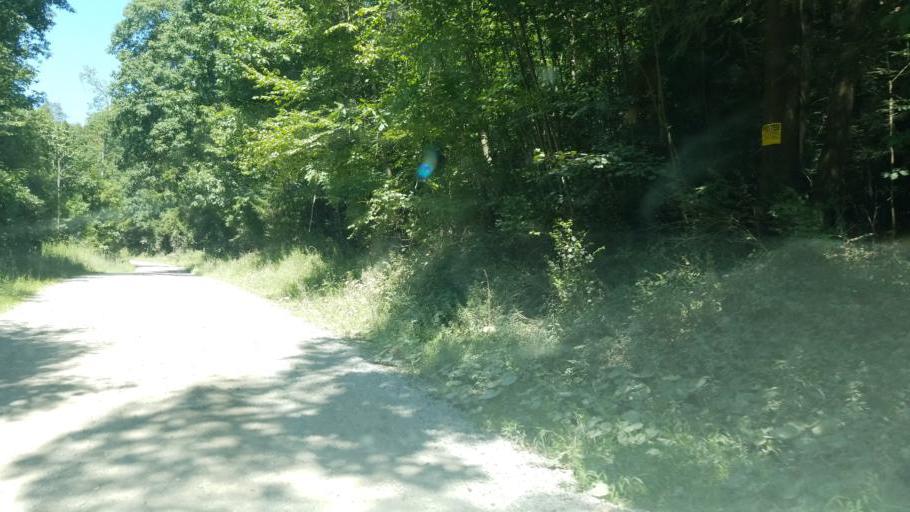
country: US
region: Pennsylvania
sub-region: Clarion County
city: Clarion
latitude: 41.1760
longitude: -79.4453
